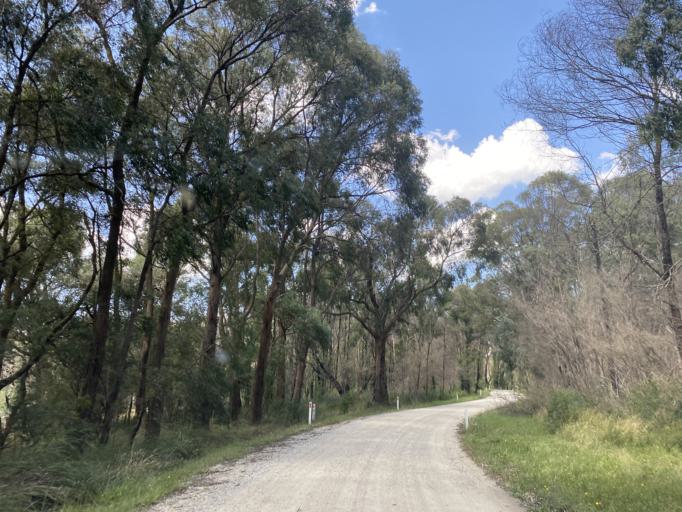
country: AU
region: Victoria
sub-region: Cardinia
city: Bunyip
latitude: -38.0047
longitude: 145.7230
